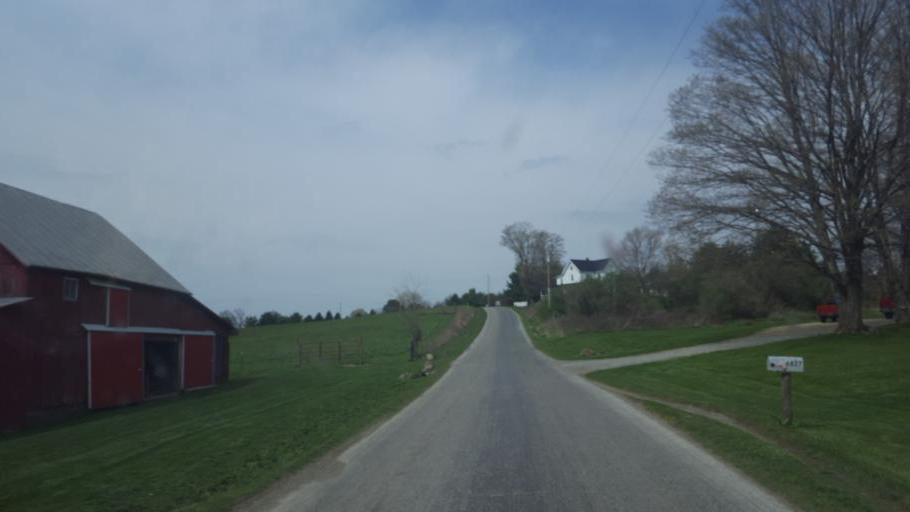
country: US
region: Ohio
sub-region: Knox County
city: Fredericktown
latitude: 40.5183
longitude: -82.6176
